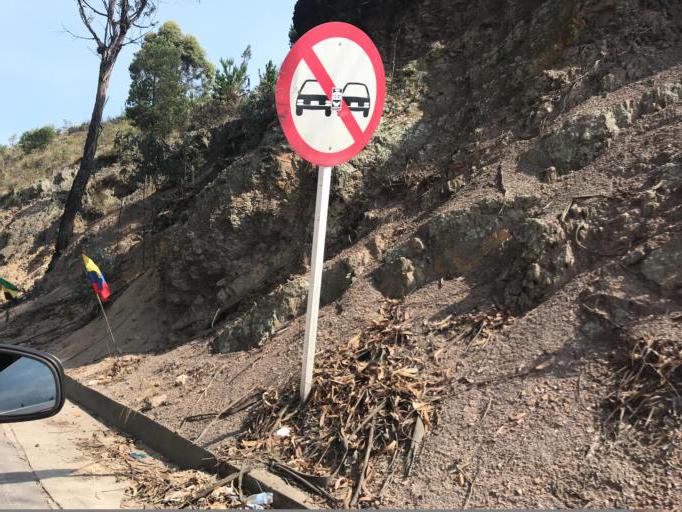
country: CO
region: Boyaca
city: Samaca
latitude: 5.4870
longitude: -73.4804
